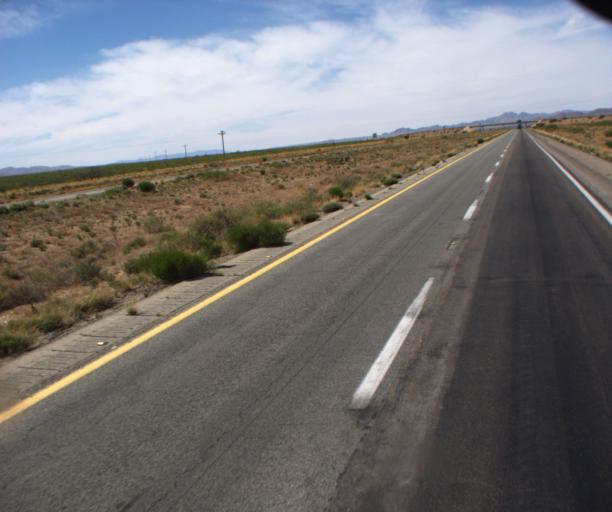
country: US
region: Arizona
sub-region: Cochise County
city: Willcox
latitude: 32.3254
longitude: -109.5062
